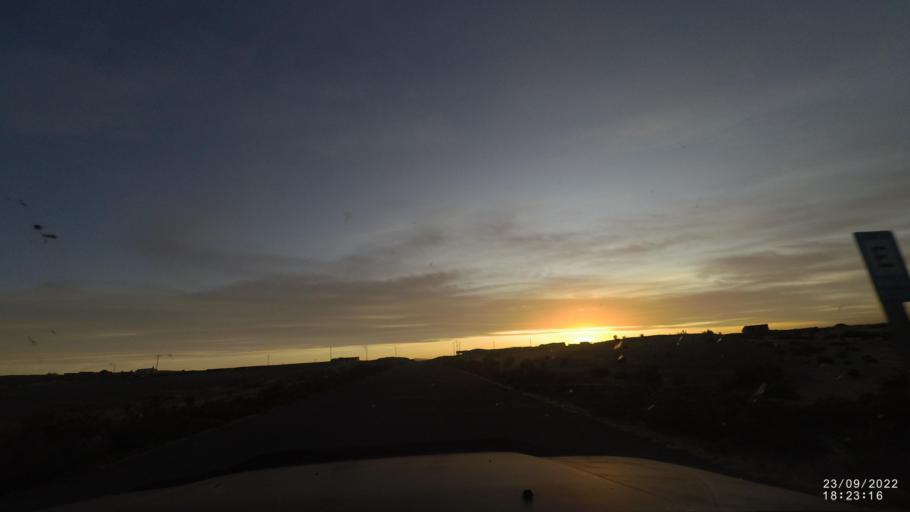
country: BO
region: Oruro
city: Challapata
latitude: -19.2941
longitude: -67.1003
